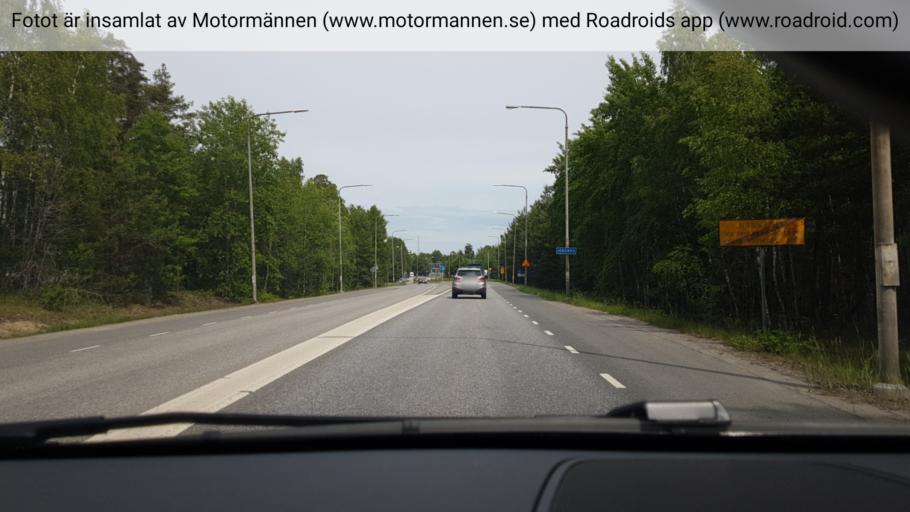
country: SE
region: Stockholm
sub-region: Haninge Kommun
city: Jordbro
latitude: 59.1368
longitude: 18.1223
